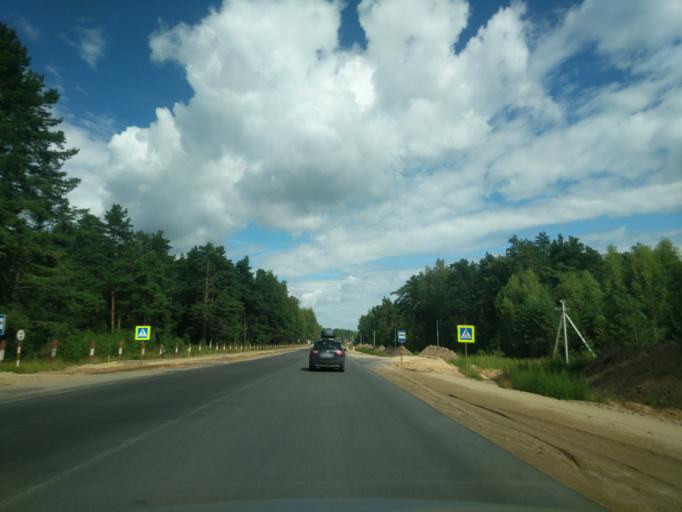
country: RU
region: Jaroslavl
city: Levashevo
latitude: 57.6669
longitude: 40.5758
